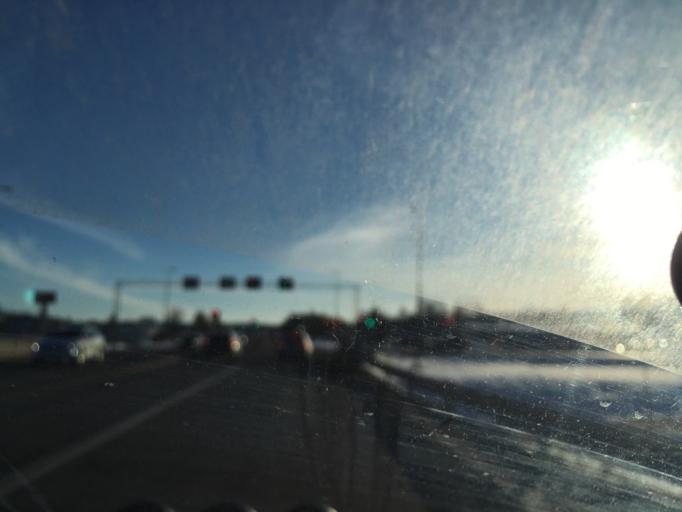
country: SE
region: Dalarna
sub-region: Borlange Kommun
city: Borlaenge
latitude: 60.4773
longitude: 15.4083
